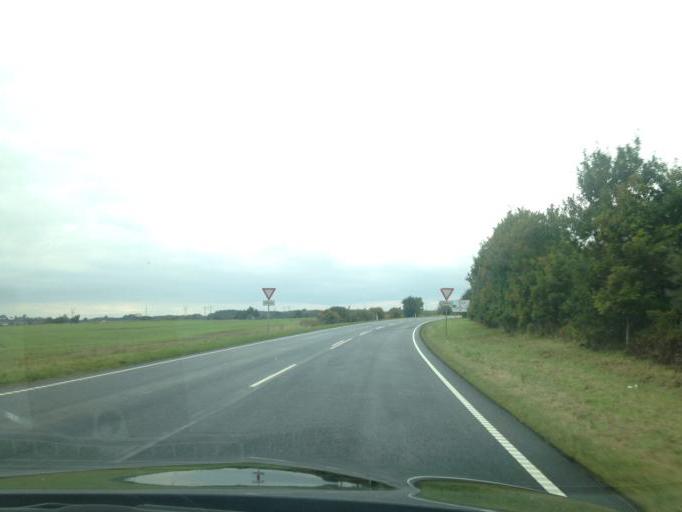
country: DK
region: South Denmark
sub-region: Kolding Kommune
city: Christiansfeld
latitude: 55.3516
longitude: 9.4782
